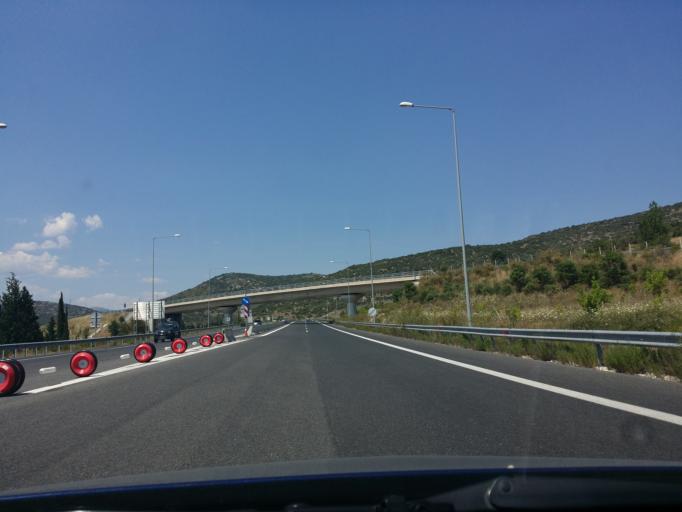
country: GR
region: Peloponnese
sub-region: Nomos Arkadias
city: Tripoli
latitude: 37.4150
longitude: 22.3085
